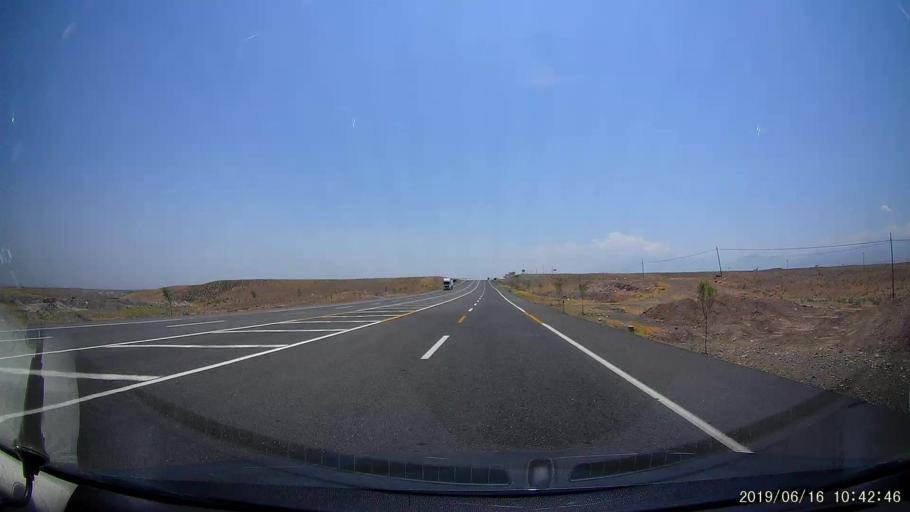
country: AM
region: Armavir
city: Shenavan
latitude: 40.0394
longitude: 43.8140
